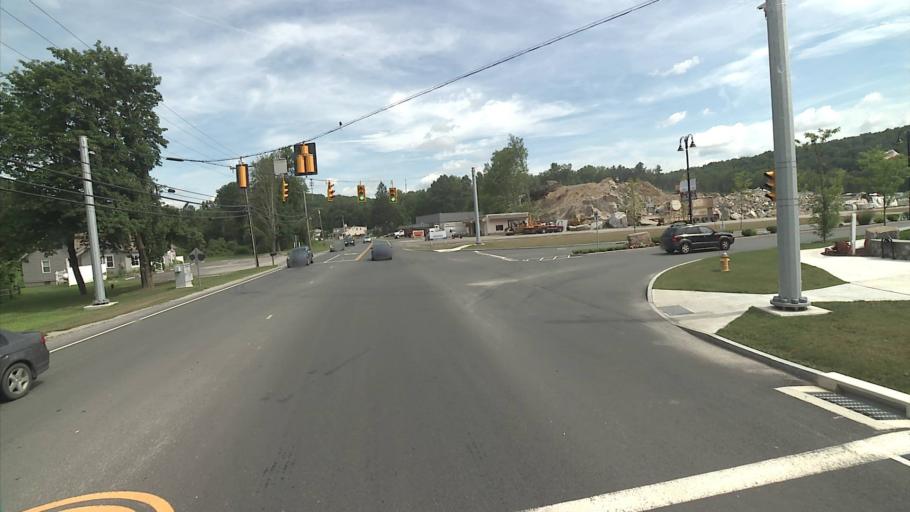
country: US
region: Connecticut
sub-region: New Haven County
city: Oxford
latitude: 41.4233
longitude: -73.1087
